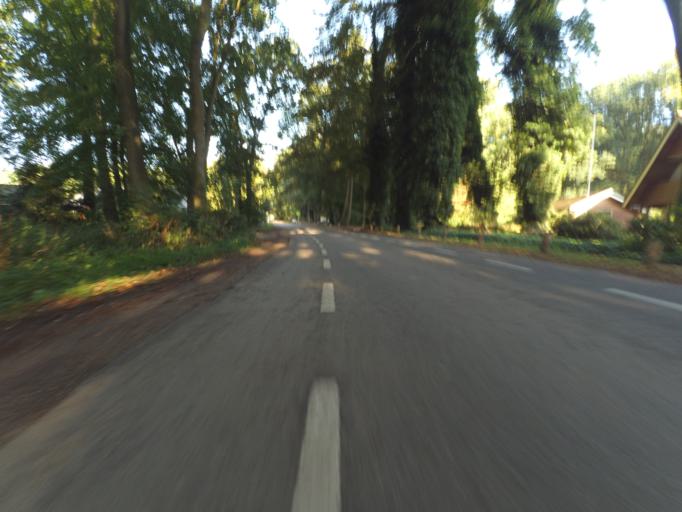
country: NL
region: Gelderland
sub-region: Gemeente Epe
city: Vaassen
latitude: 52.2900
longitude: 5.9426
